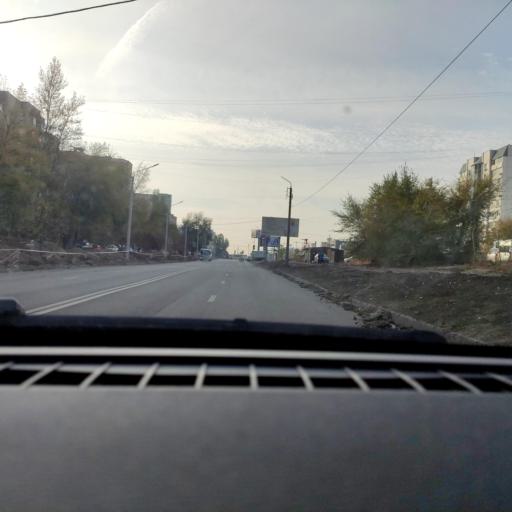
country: RU
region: Voronezj
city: Podgornoye
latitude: 51.7150
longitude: 39.1618
